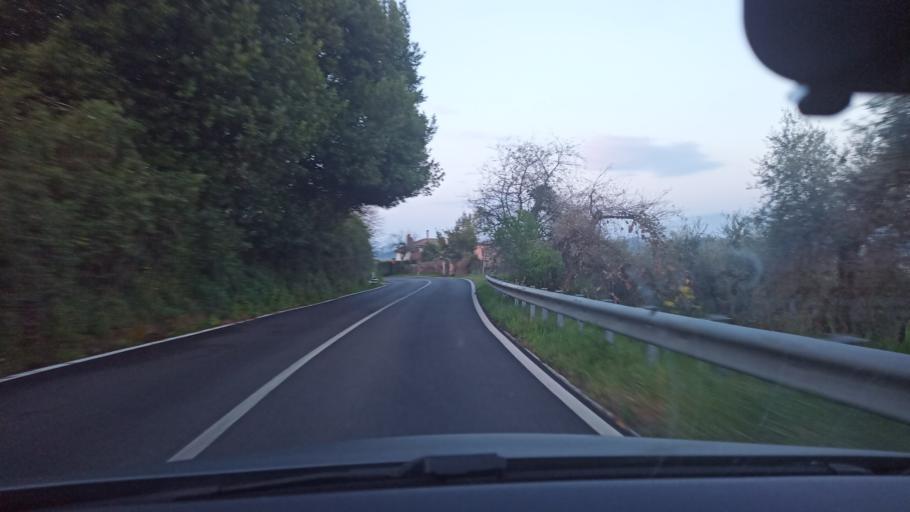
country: IT
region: Latium
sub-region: Provincia di Rieti
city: Torri in Sabina
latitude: 42.3344
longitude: 12.6455
